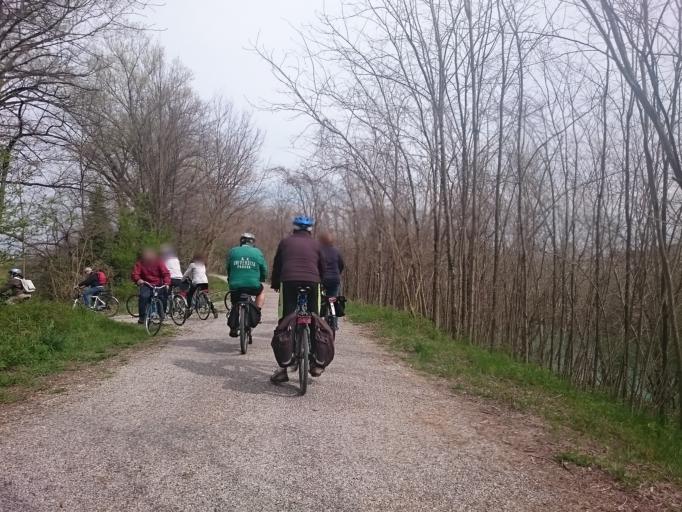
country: IT
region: Veneto
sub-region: Provincia di Padova
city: Saletto
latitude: 45.4537
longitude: 11.8636
